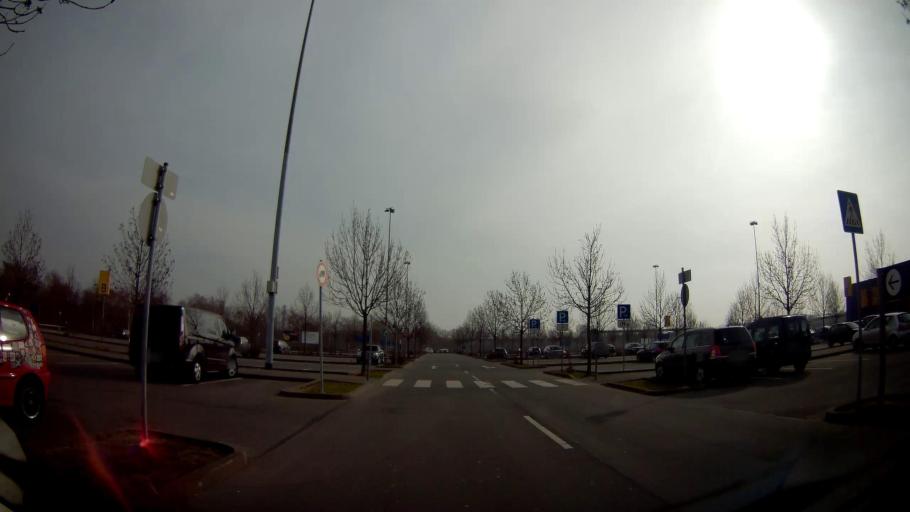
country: DE
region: North Rhine-Westphalia
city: Meiderich
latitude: 51.4833
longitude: 6.7651
